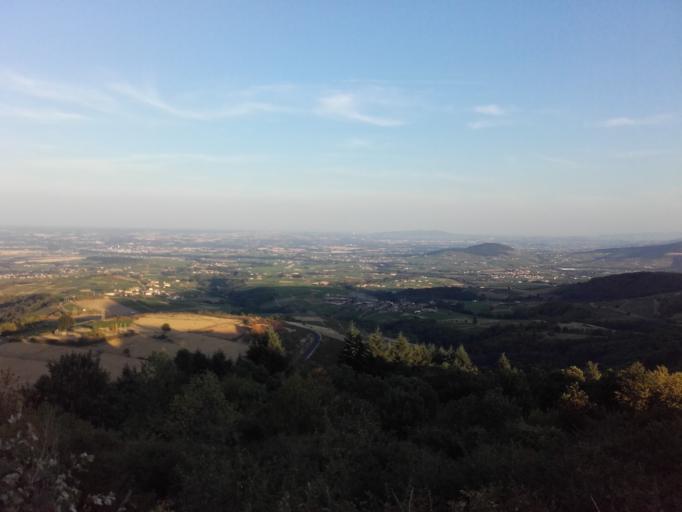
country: FR
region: Rhone-Alpes
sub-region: Departement du Rhone
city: Beaujeu
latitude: 46.1891
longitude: 4.6291
